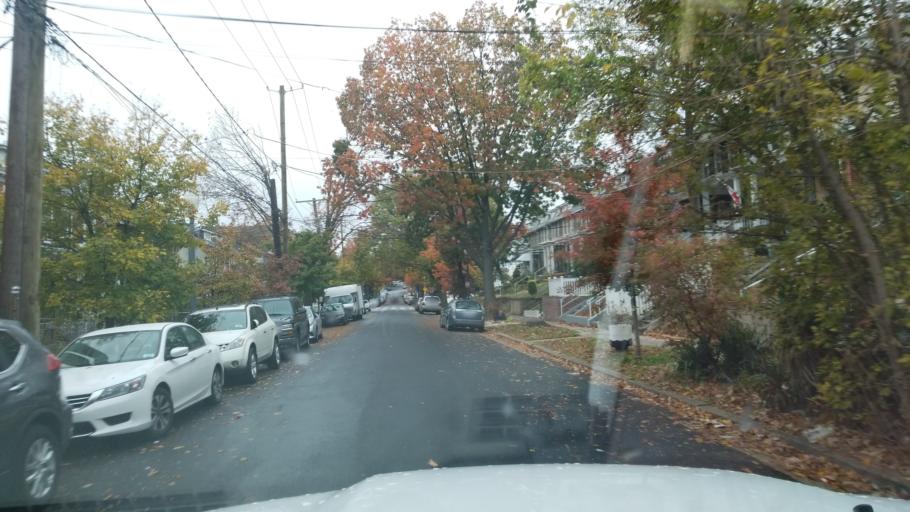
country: US
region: Maryland
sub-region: Montgomery County
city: Takoma Park
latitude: 38.9574
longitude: -77.0246
